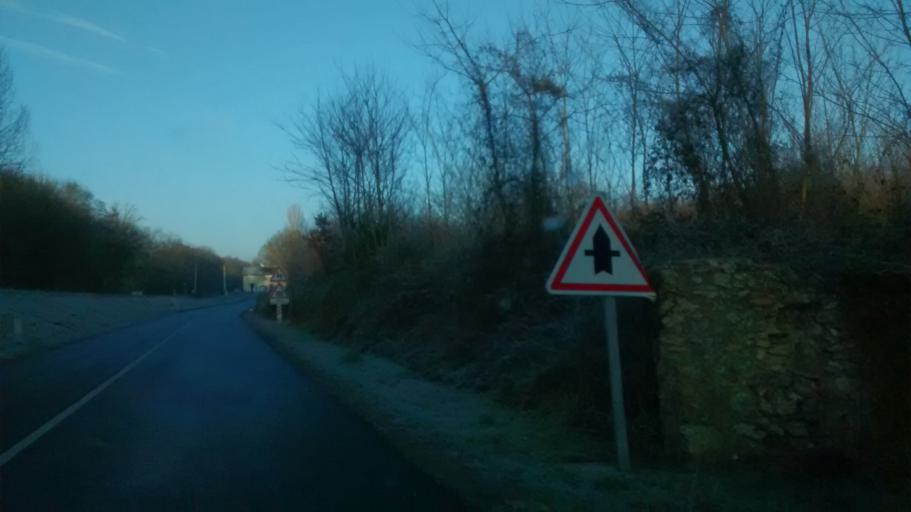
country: FR
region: Centre
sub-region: Departement d'Indre-et-Loire
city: Veigne
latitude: 47.2903
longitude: 0.7547
